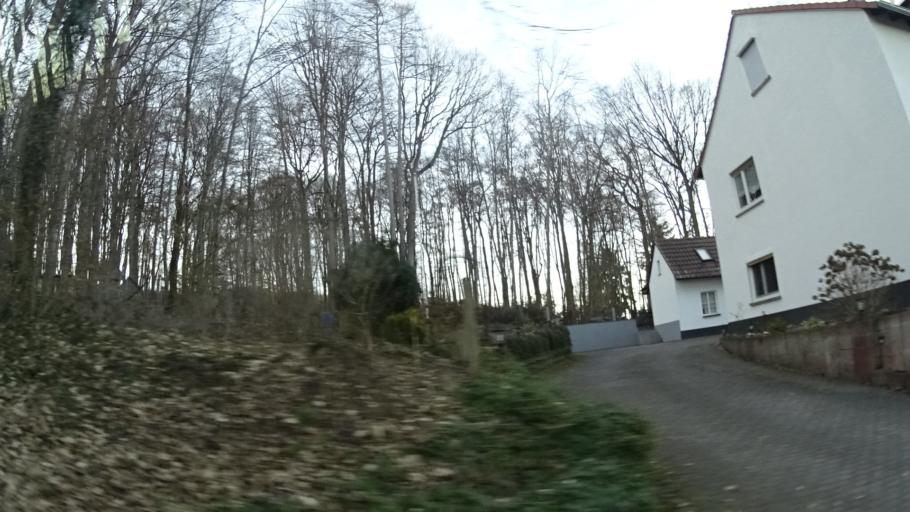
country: DE
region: Bavaria
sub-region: Regierungsbezirk Unterfranken
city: Geiselbach
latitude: 50.1218
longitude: 9.1909
